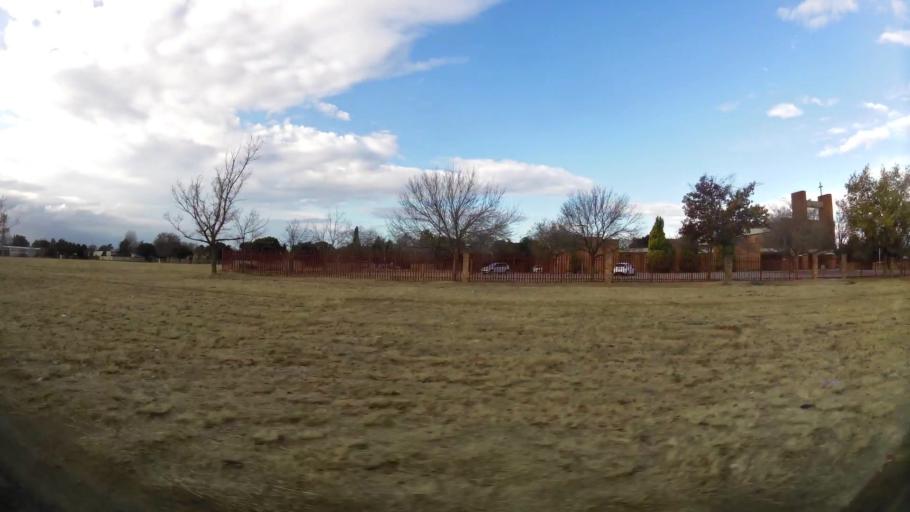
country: ZA
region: Orange Free State
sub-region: Lejweleputswa District Municipality
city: Welkom
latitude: -27.9981
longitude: 26.7340
